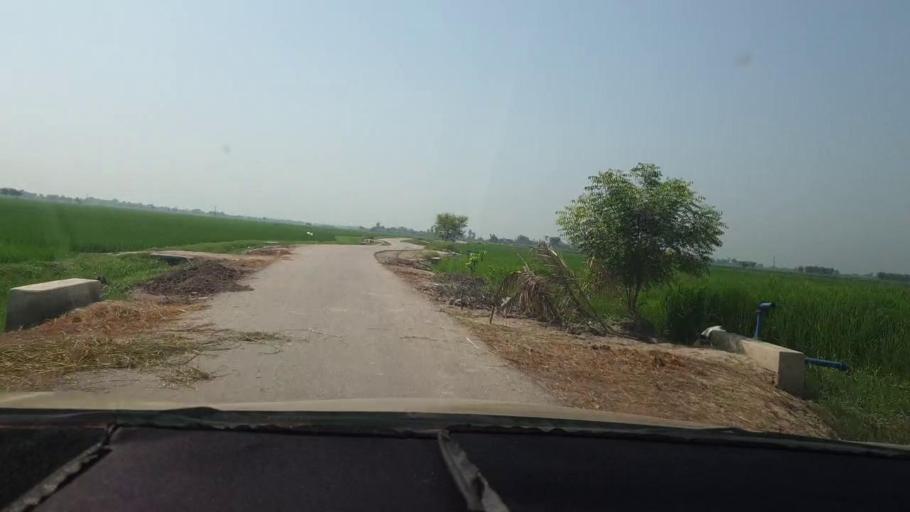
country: PK
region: Sindh
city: Kambar
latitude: 27.5669
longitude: 68.0445
